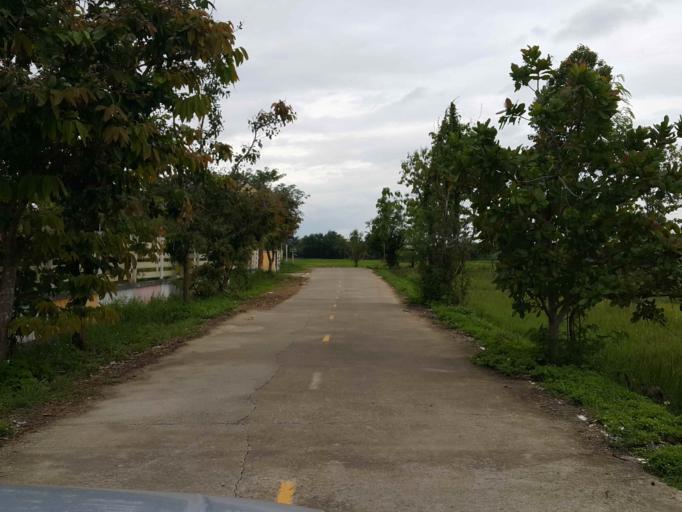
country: TH
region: Chiang Mai
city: San Sai
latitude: 18.8223
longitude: 99.0718
